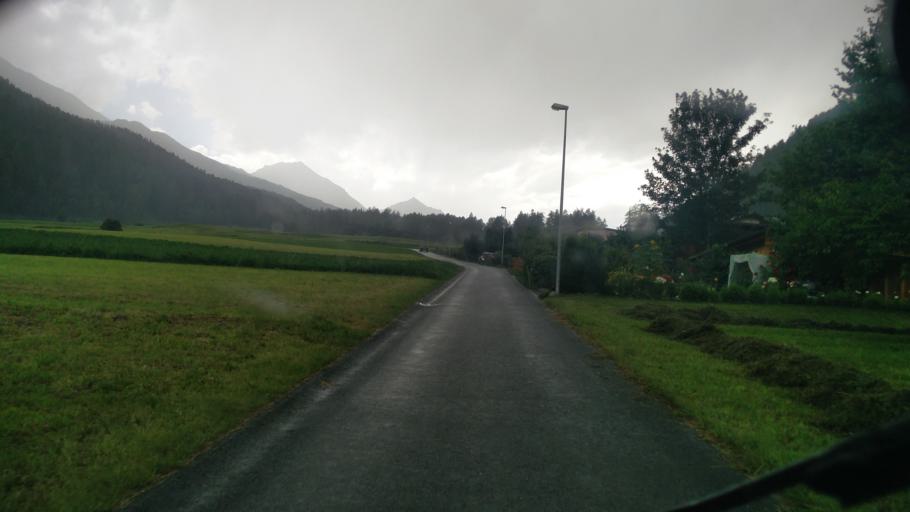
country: IT
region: Trentino-Alto Adige
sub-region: Bolzano
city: Tubre
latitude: 46.6007
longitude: 10.4043
